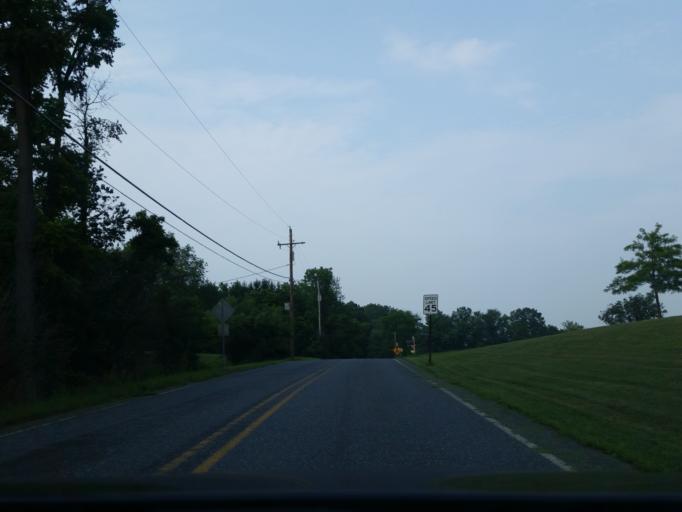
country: US
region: Pennsylvania
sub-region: Lebanon County
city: Jonestown
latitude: 40.4175
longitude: -76.5392
